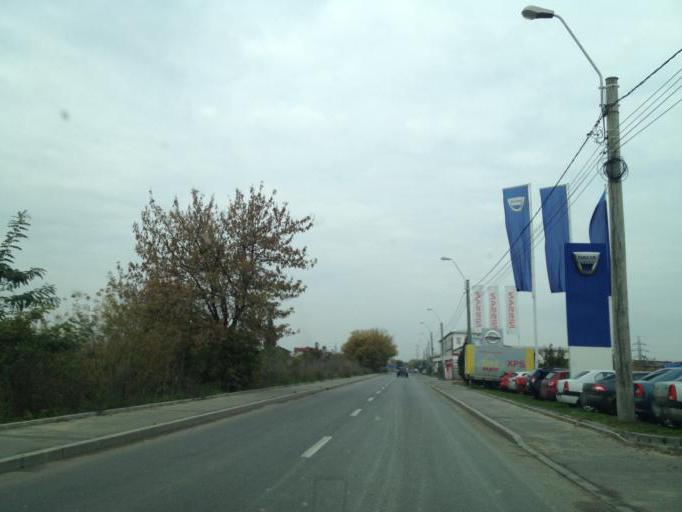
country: RO
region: Dolj
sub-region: Municipiul Craiova
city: Popoveni
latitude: 44.2925
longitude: 23.7909
